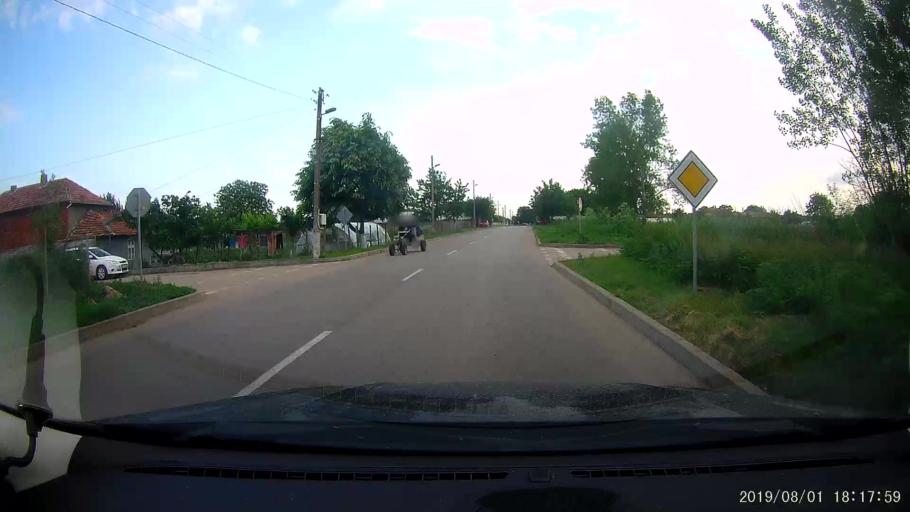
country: BG
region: Shumen
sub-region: Obshtina Kaolinovo
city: Kaolinovo
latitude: 43.7032
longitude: 27.0807
